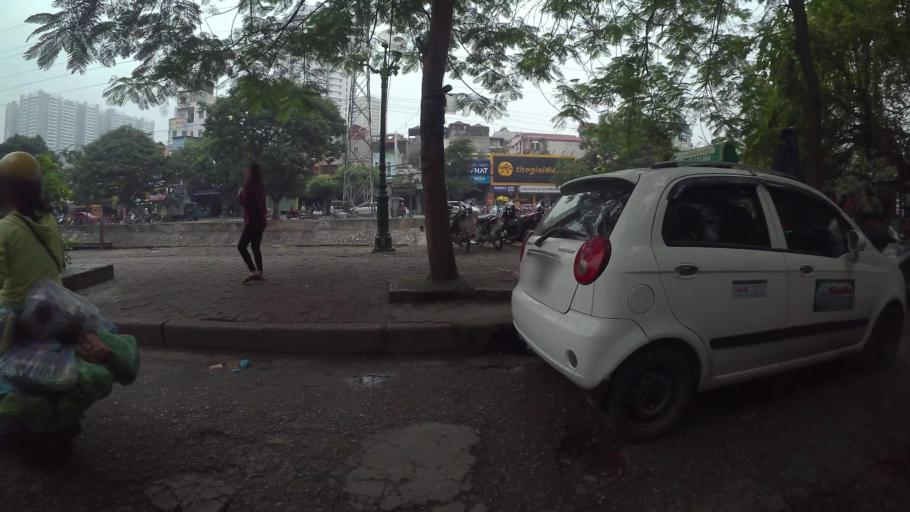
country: VN
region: Ha Noi
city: Hai BaTrung
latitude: 20.9884
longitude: 105.8629
